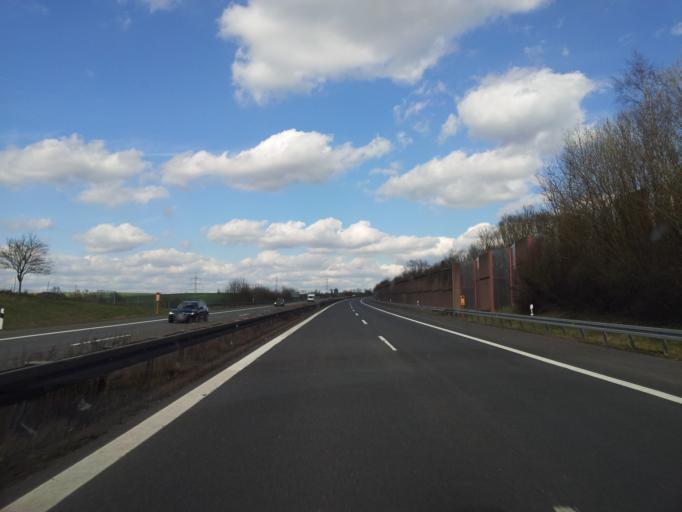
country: DE
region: Bavaria
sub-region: Upper Franconia
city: Memmelsdorf
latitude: 49.9454
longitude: 10.9662
